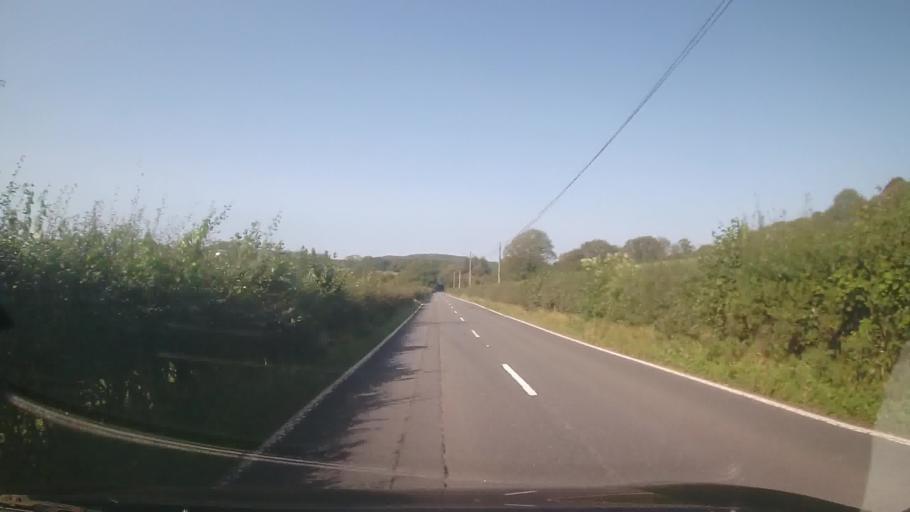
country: GB
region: Wales
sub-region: Sir Powys
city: Builth Wells
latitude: 52.1394
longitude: -3.5648
